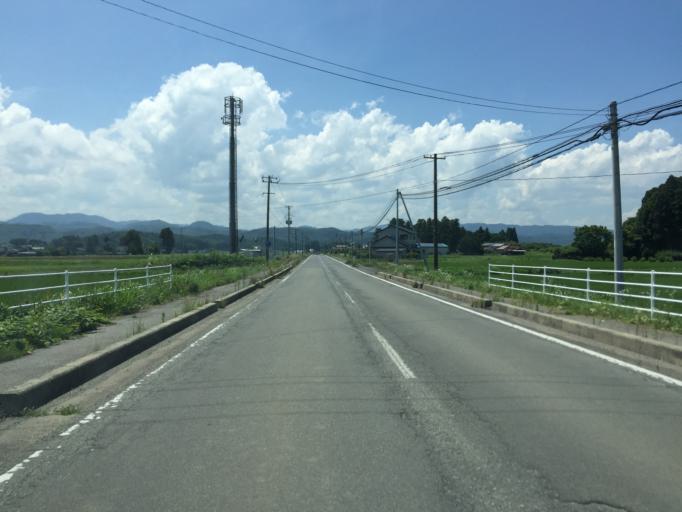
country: JP
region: Fukushima
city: Namie
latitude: 37.7122
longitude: 140.9535
